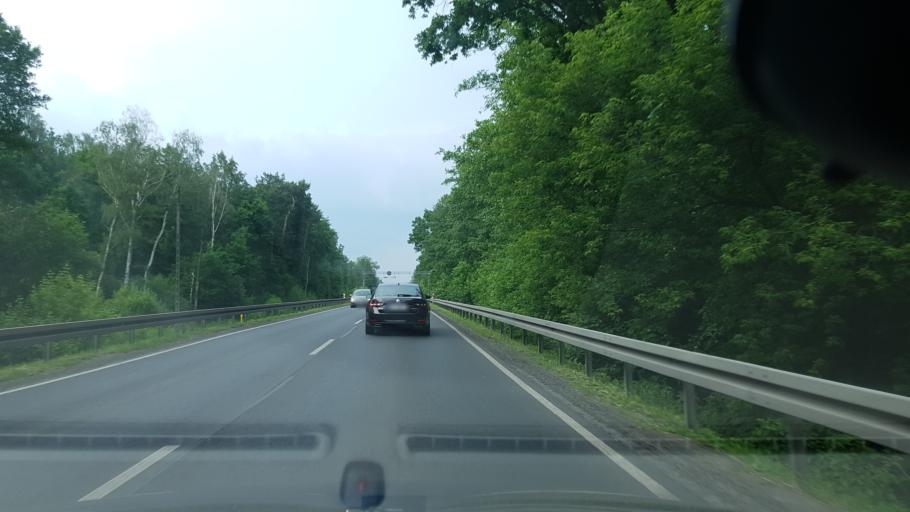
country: PL
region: Masovian Voivodeship
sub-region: Powiat legionowski
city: Wieliszew
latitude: 52.4406
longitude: 20.9959
